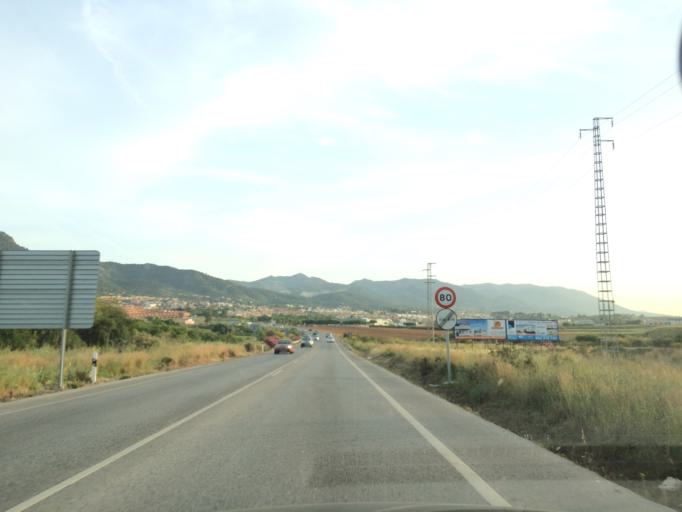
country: ES
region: Andalusia
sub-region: Provincia de Malaga
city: Alhaurin de la Torre
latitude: 36.6749
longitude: -4.5344
